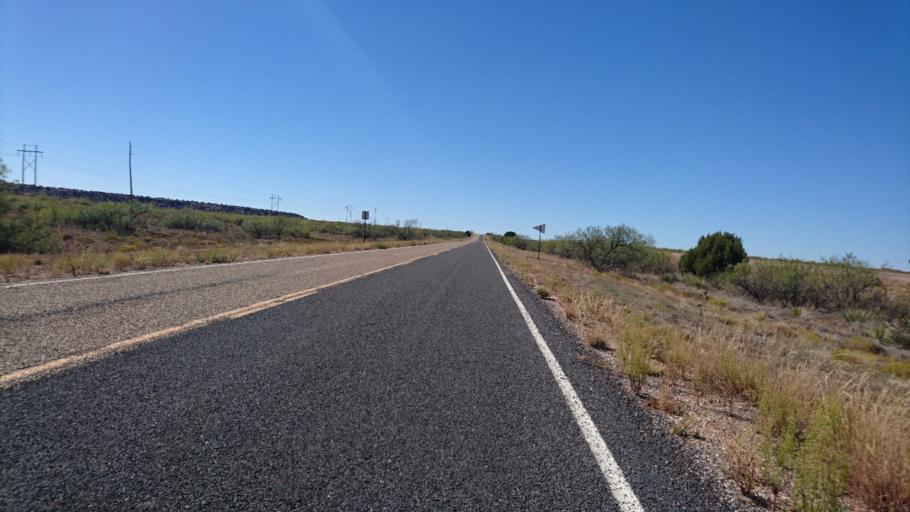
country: US
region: New Mexico
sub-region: Quay County
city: Tucumcari
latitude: 35.0813
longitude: -104.1173
